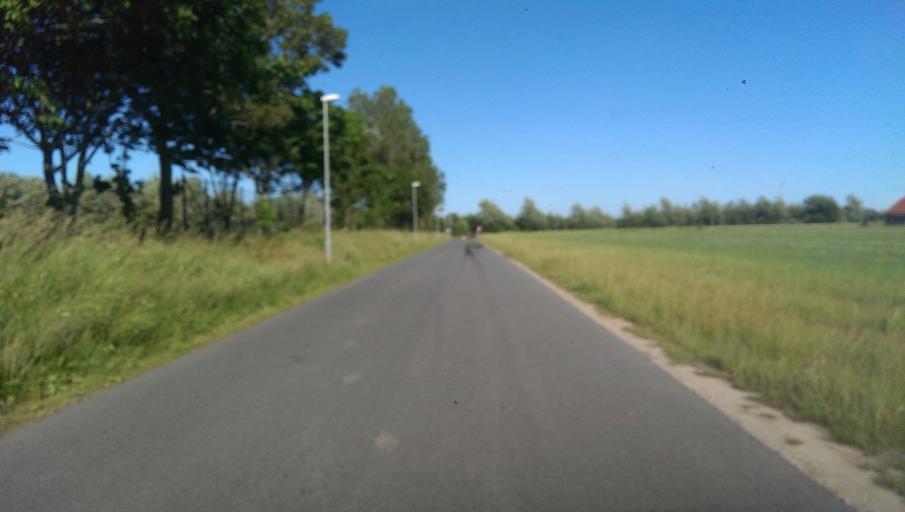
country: DK
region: South Denmark
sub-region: Esbjerg Kommune
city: Esbjerg
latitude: 55.5201
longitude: 8.4030
